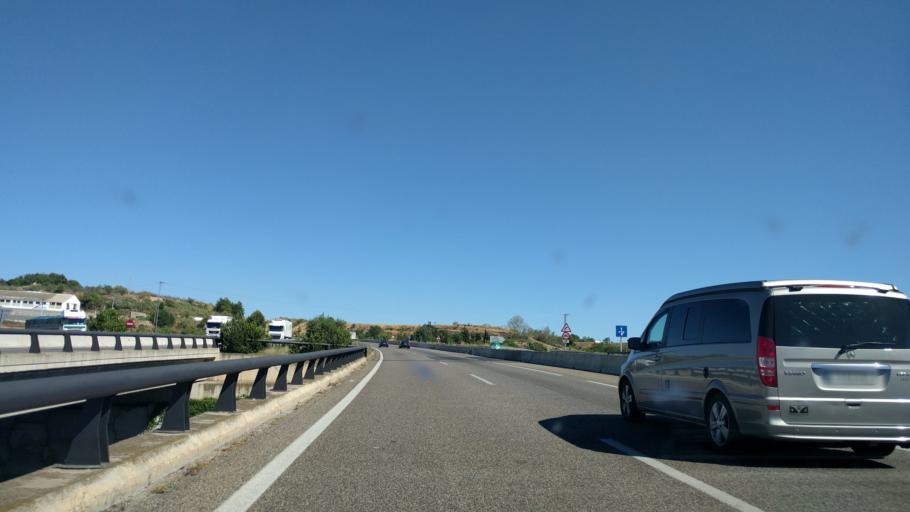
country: ES
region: Catalonia
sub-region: Provincia de Lleida
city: Alcoletge
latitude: 41.6415
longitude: 0.6756
